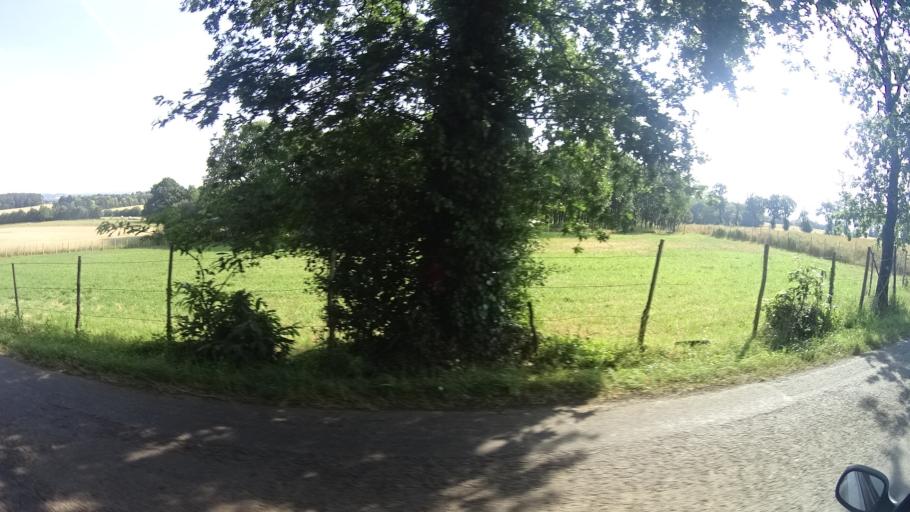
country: FR
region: Brittany
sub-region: Departement d'Ille-et-Vilaine
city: Sixt-sur-Aff
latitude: 47.7649
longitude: -2.0706
